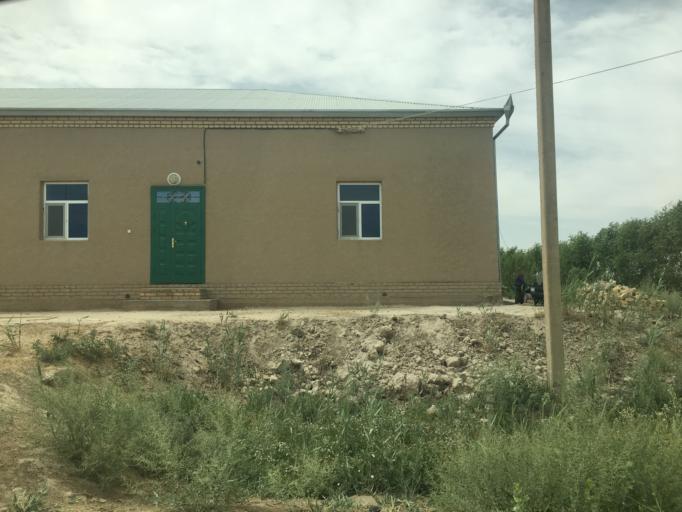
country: TM
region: Dasoguz
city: Tagta
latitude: 41.6136
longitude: 59.8217
